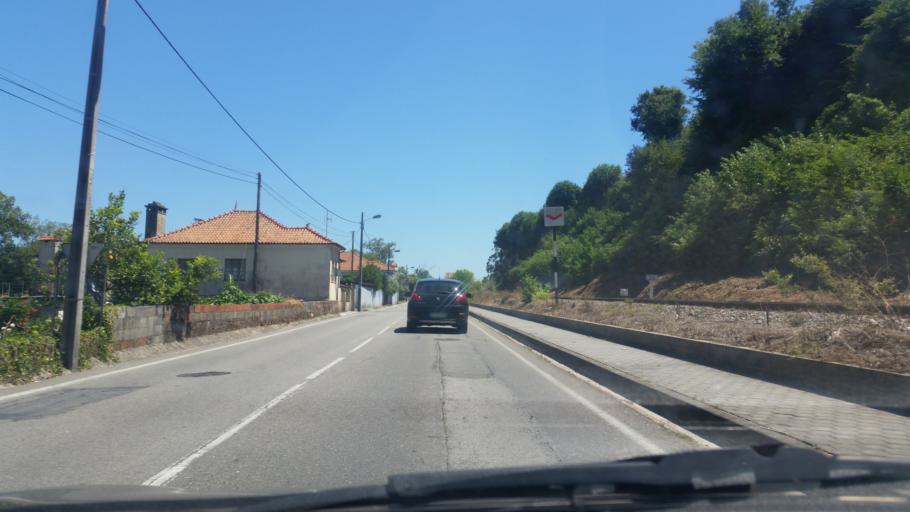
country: PT
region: Aveiro
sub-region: Aveiro
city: Eixo
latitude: 40.6112
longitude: -8.5333
